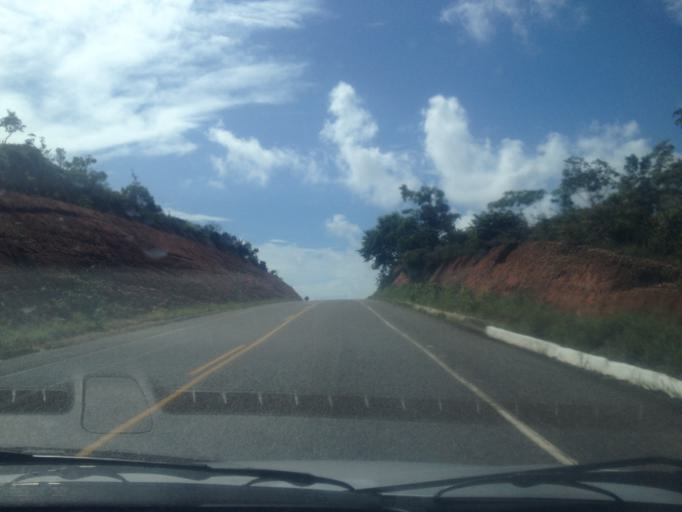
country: BR
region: Bahia
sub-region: Conde
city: Conde
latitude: -11.9136
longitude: -37.6596
